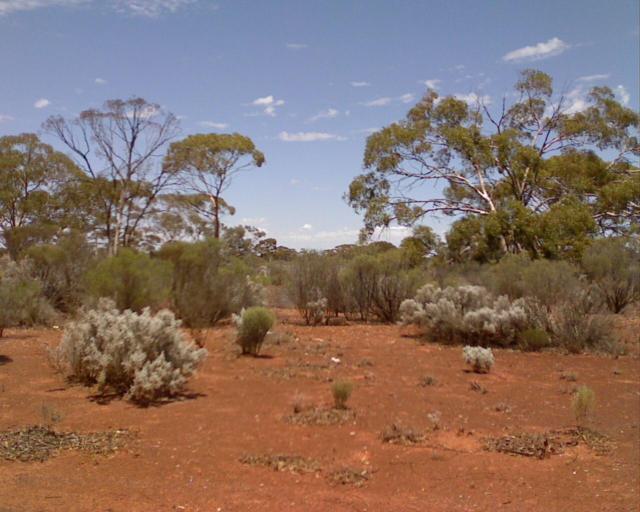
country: AU
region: Western Australia
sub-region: Kalgoorlie/Boulder
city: Boulder
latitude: -30.9429
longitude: 121.5555
